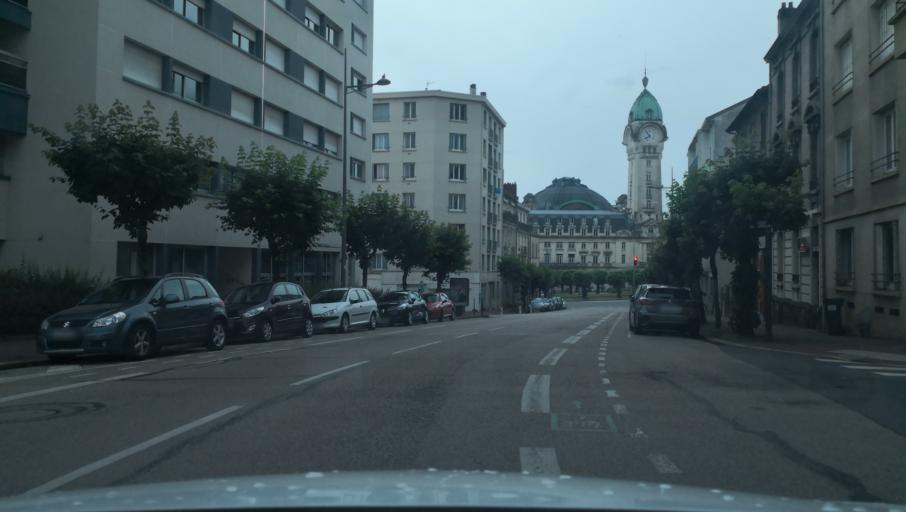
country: FR
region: Limousin
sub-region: Departement de la Haute-Vienne
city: Limoges
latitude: 45.8377
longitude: 1.2650
